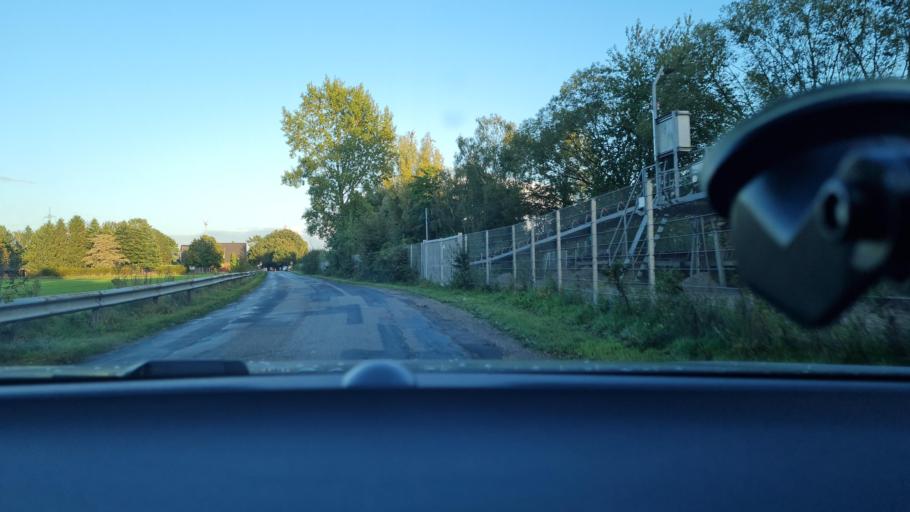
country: DE
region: North Rhine-Westphalia
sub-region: Regierungsbezirk Dusseldorf
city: Dinslaken
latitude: 51.5924
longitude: 6.7254
